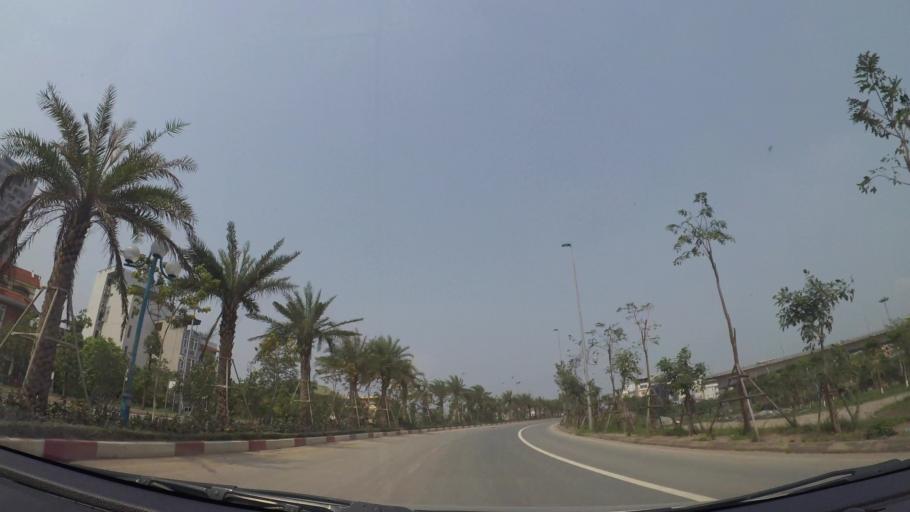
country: VN
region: Ha Noi
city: Tay Ho
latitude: 21.0851
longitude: 105.8147
